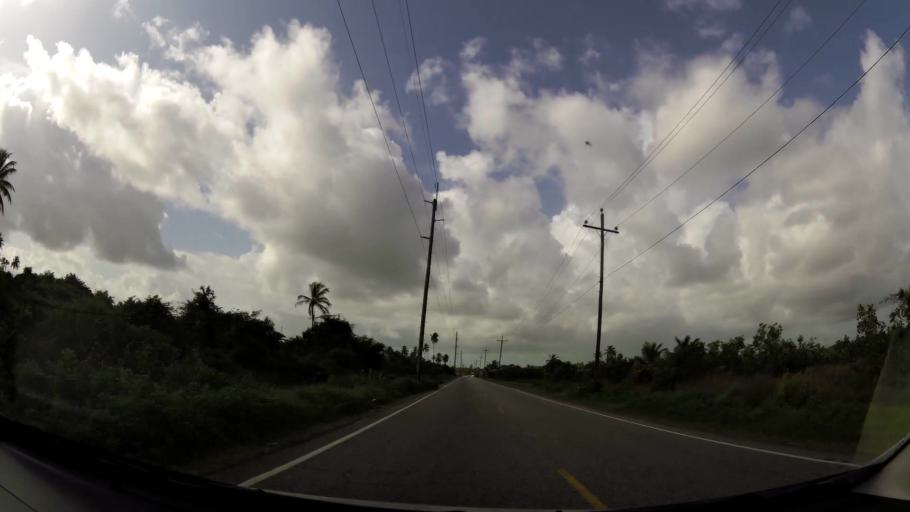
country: GY
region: Demerara-Mahaica
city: Mahaica Village
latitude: 6.6880
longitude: -57.9288
